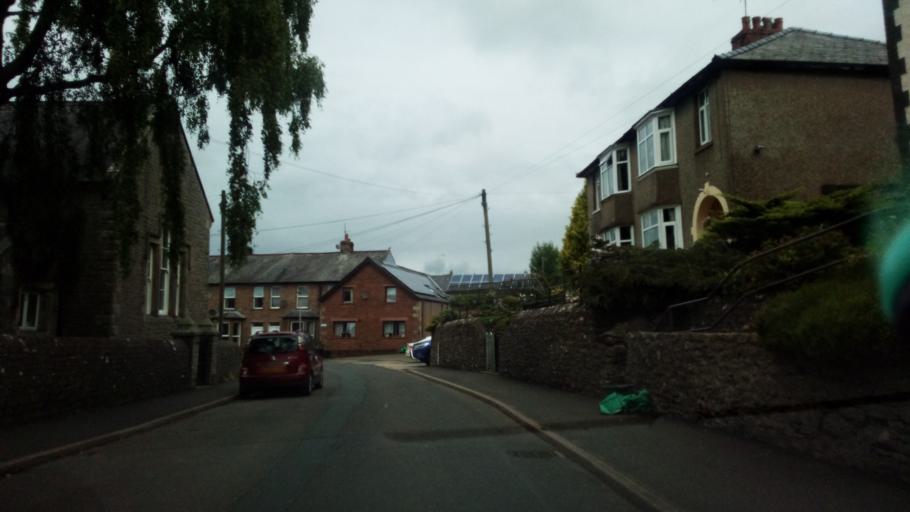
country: GB
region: England
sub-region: Cumbria
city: Kirkby Stephen
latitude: 54.4703
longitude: -2.3470
